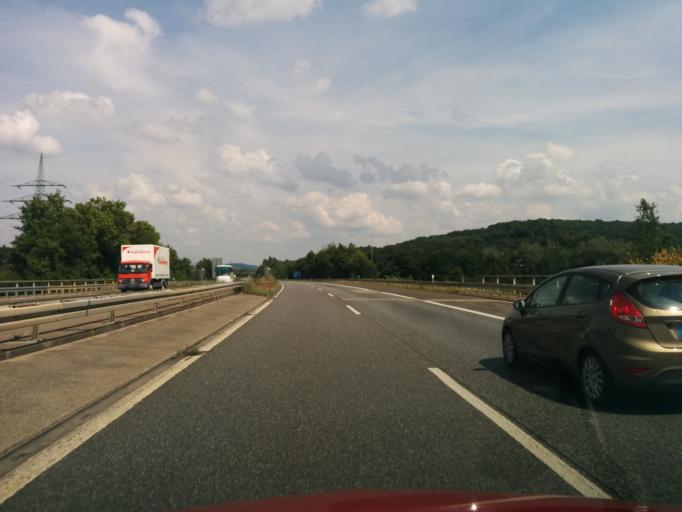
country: DE
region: Hesse
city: Lollar
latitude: 50.6269
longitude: 8.7068
